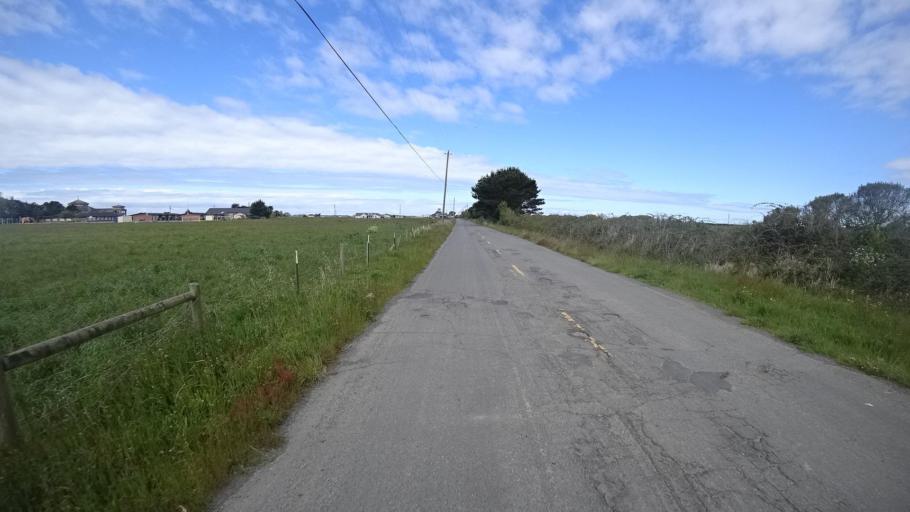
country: US
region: California
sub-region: Humboldt County
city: Arcata
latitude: 40.8802
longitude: -124.0974
